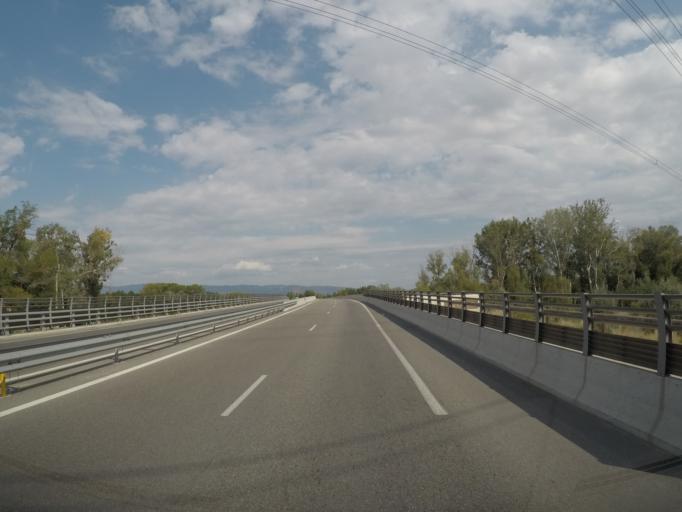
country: FR
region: Provence-Alpes-Cote d'Azur
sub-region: Departement du Vaucluse
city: Pertuis
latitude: 43.6651
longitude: 5.4958
